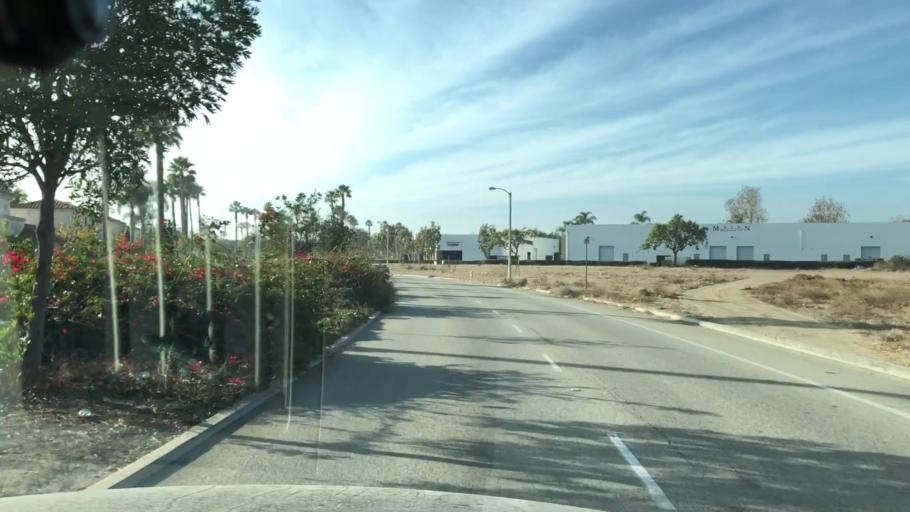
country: US
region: California
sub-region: Ventura County
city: El Rio
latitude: 34.2261
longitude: -119.1439
